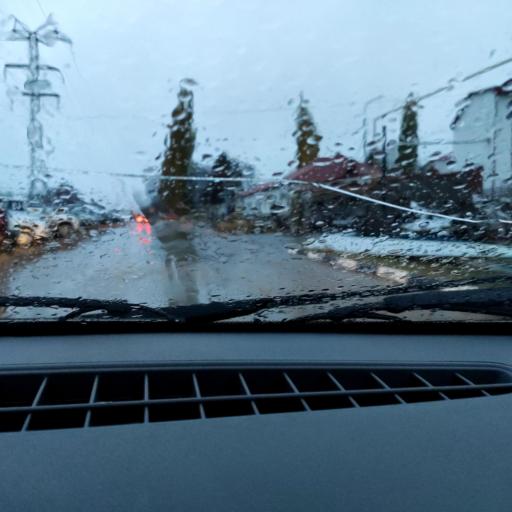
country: RU
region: Bashkortostan
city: Avdon
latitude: 54.6852
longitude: 55.8042
